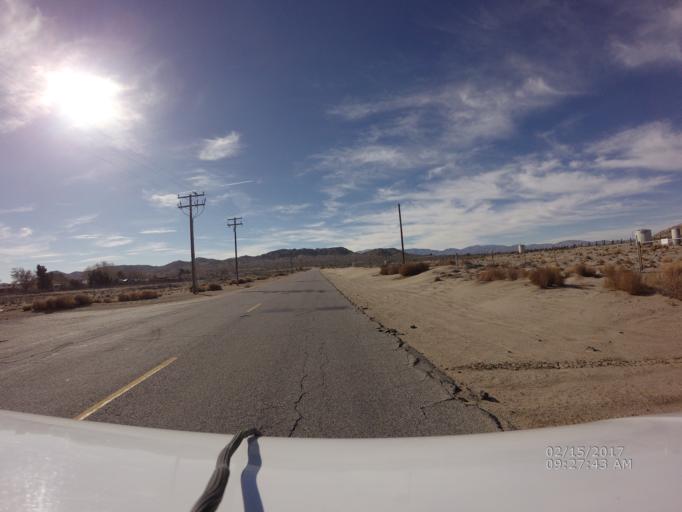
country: US
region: California
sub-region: Los Angeles County
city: Lake Los Angeles
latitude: 34.6239
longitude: -117.8627
